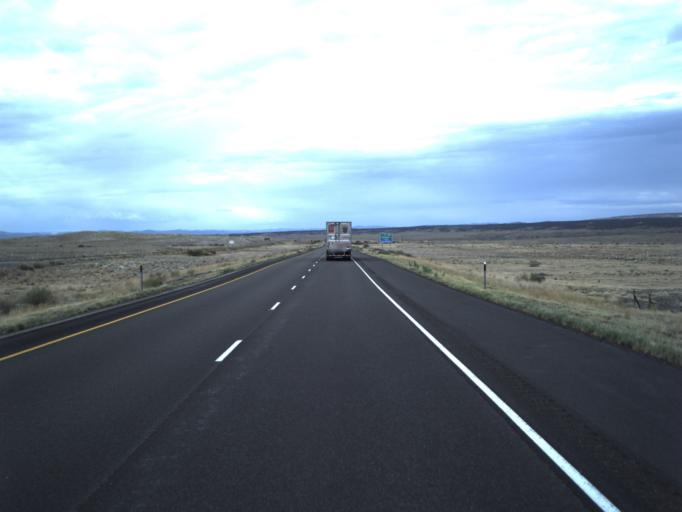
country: US
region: Colorado
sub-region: Mesa County
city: Loma
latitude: 39.0977
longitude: -109.2042
